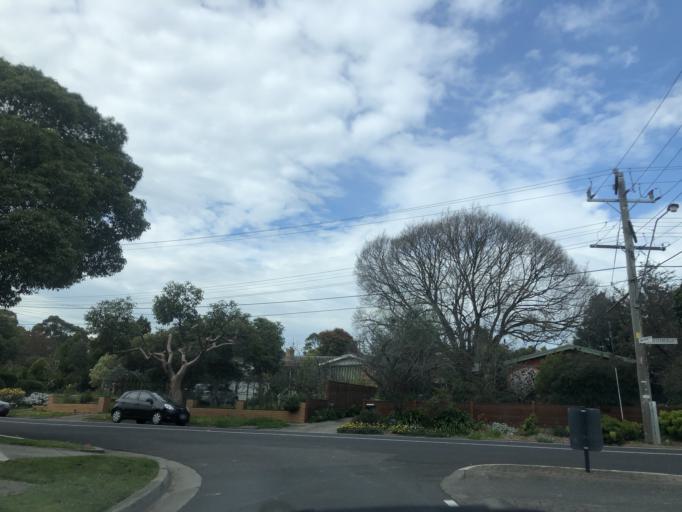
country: AU
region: Victoria
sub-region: Monash
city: Notting Hill
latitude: -37.9031
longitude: 145.1499
